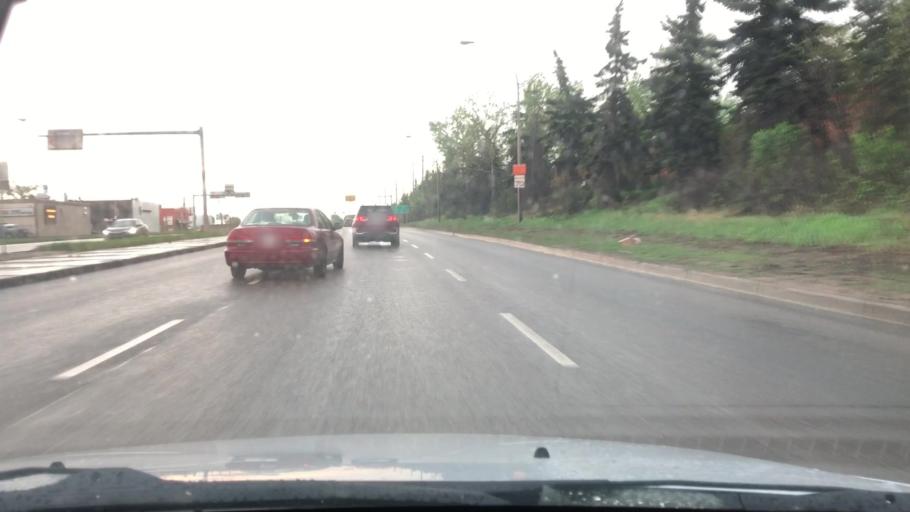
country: CA
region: Alberta
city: Edmonton
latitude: 53.5805
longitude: -113.5404
